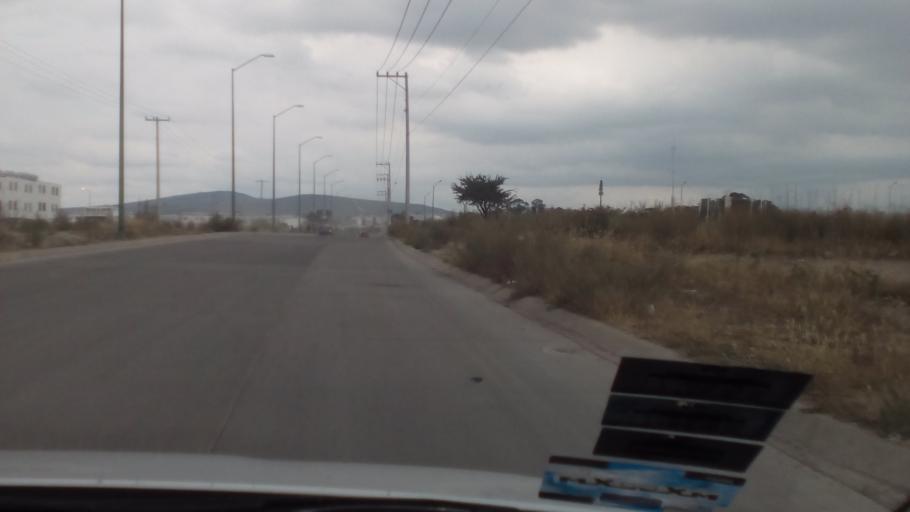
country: MX
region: Guanajuato
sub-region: Leon
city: Fraccionamiento Paseo de las Torres
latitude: 21.1803
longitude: -101.7663
